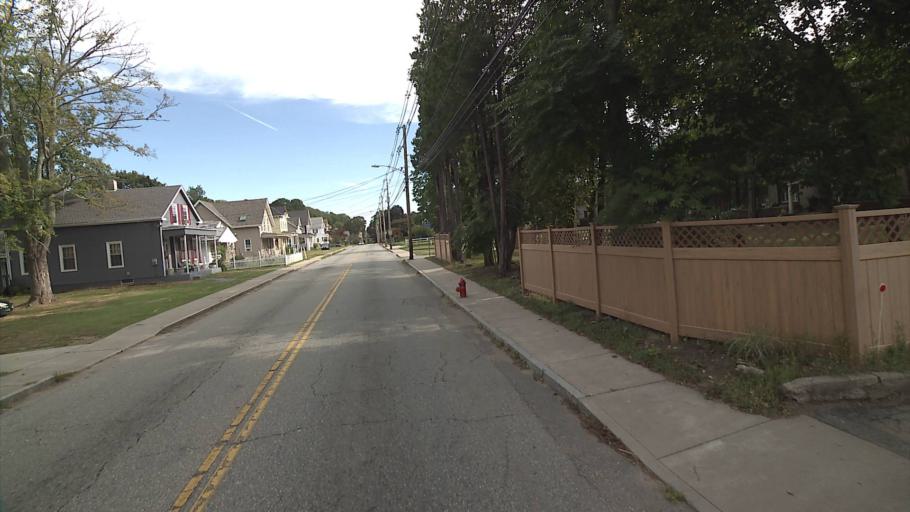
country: US
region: Connecticut
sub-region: New London County
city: Norwich
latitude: 41.5128
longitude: -72.0829
